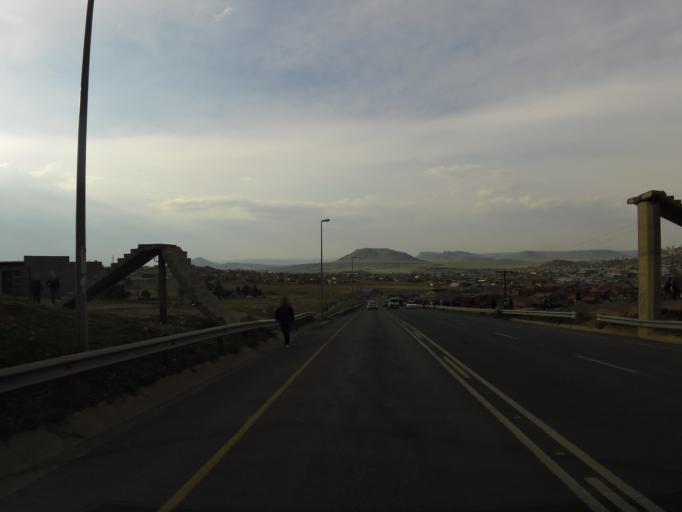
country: LS
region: Maseru
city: Maseru
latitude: -29.3527
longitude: 27.4561
